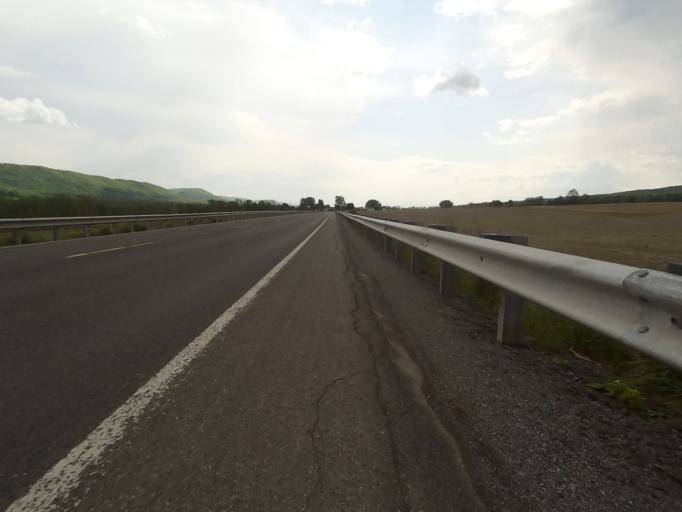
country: US
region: Pennsylvania
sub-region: Centre County
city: Zion
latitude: 40.9574
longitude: -77.6172
